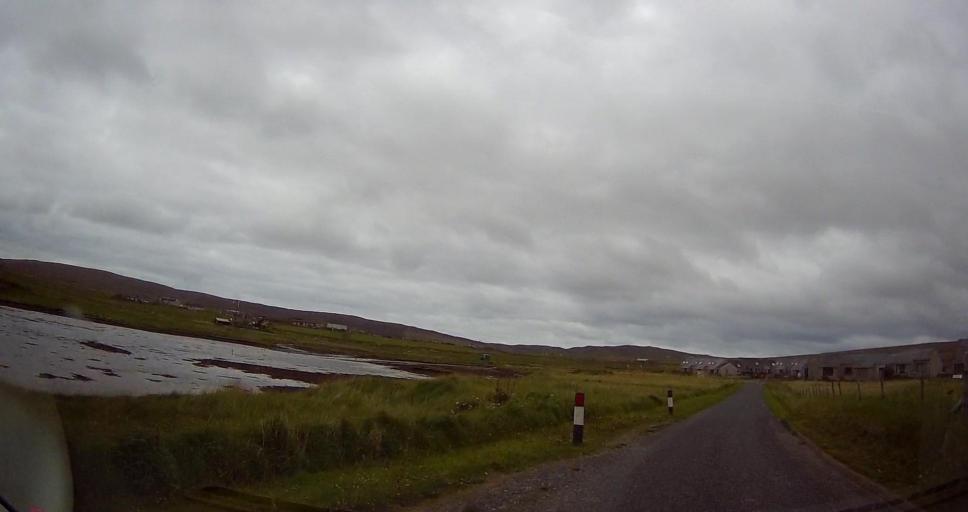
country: GB
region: Scotland
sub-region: Shetland Islands
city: Shetland
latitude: 60.7572
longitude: -0.8613
